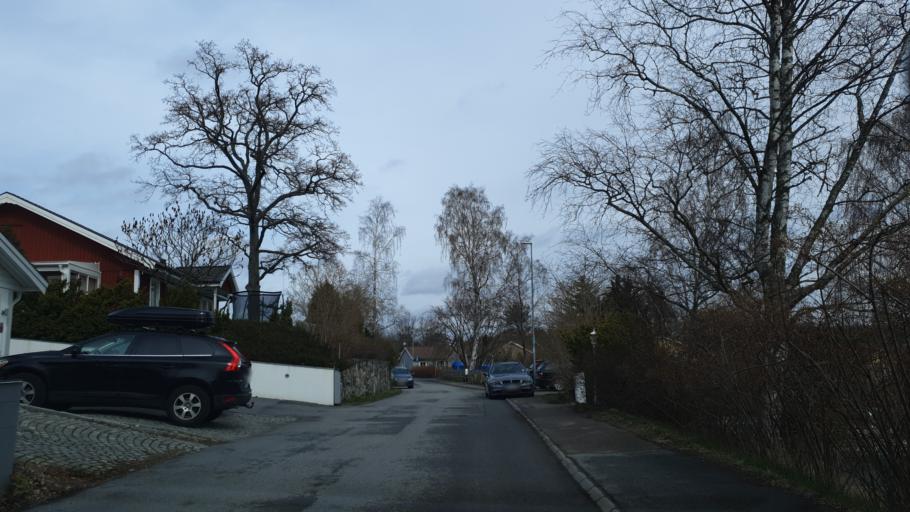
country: SE
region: Stockholm
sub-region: Nacka Kommun
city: Boo
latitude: 59.3279
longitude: 18.2755
